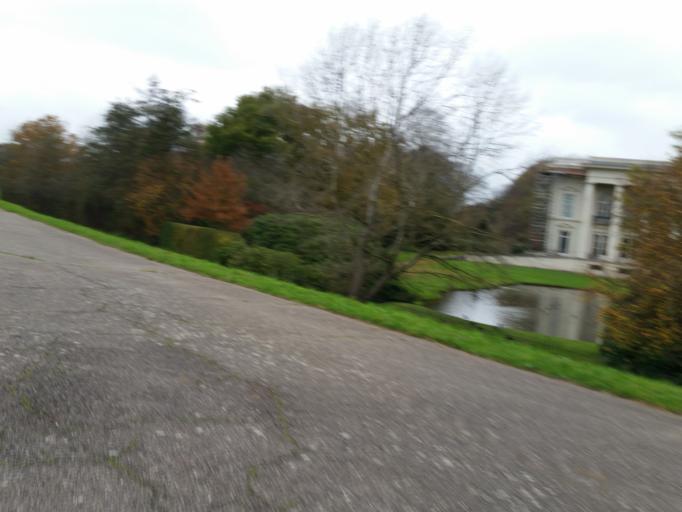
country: BE
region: Flanders
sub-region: Provincie Antwerpen
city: Lier
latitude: 51.1173
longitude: 4.5500
